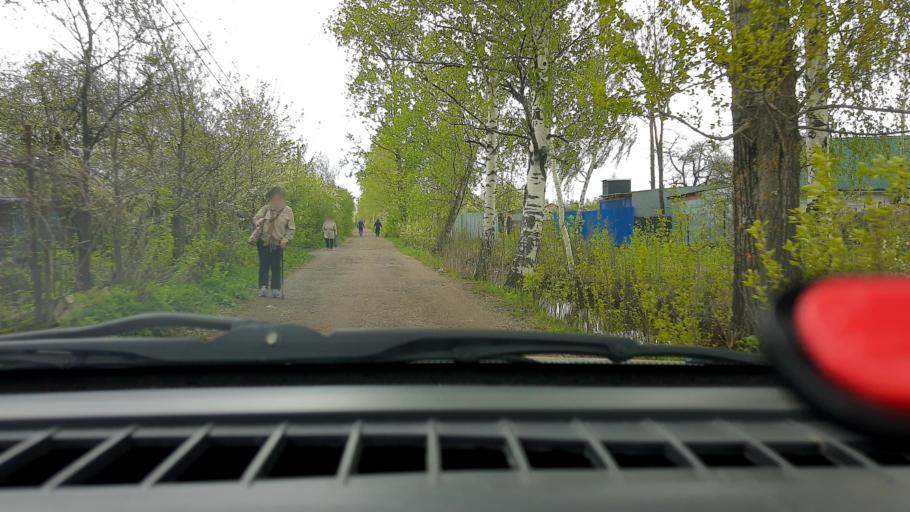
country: RU
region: Nizjnij Novgorod
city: Gorbatovka
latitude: 56.2410
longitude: 43.8135
